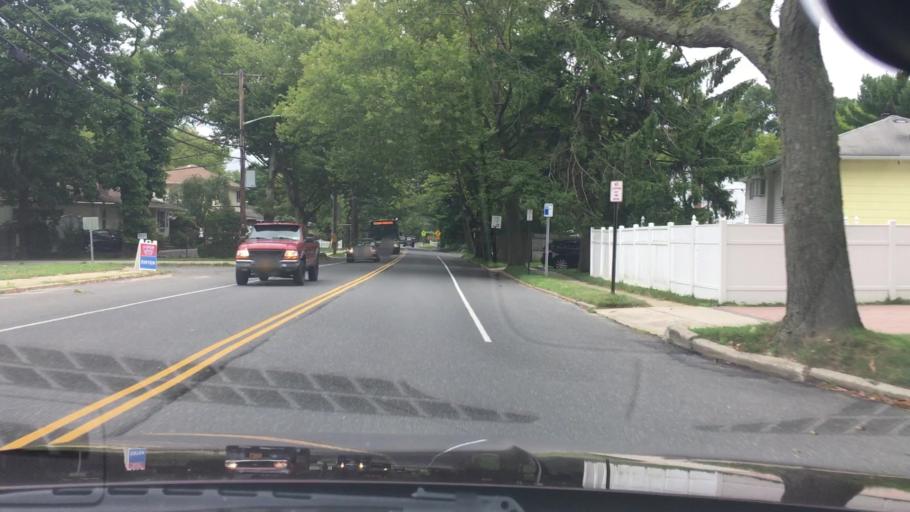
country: US
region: New York
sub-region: Suffolk County
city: South Huntington
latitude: 40.8124
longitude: -73.4006
